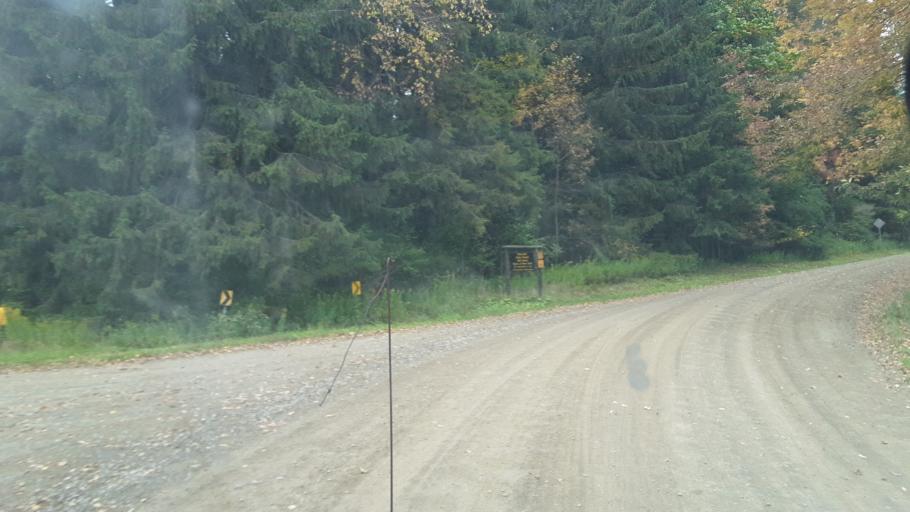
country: US
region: New York
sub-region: Allegany County
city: Alfred
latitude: 42.3694
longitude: -77.8484
